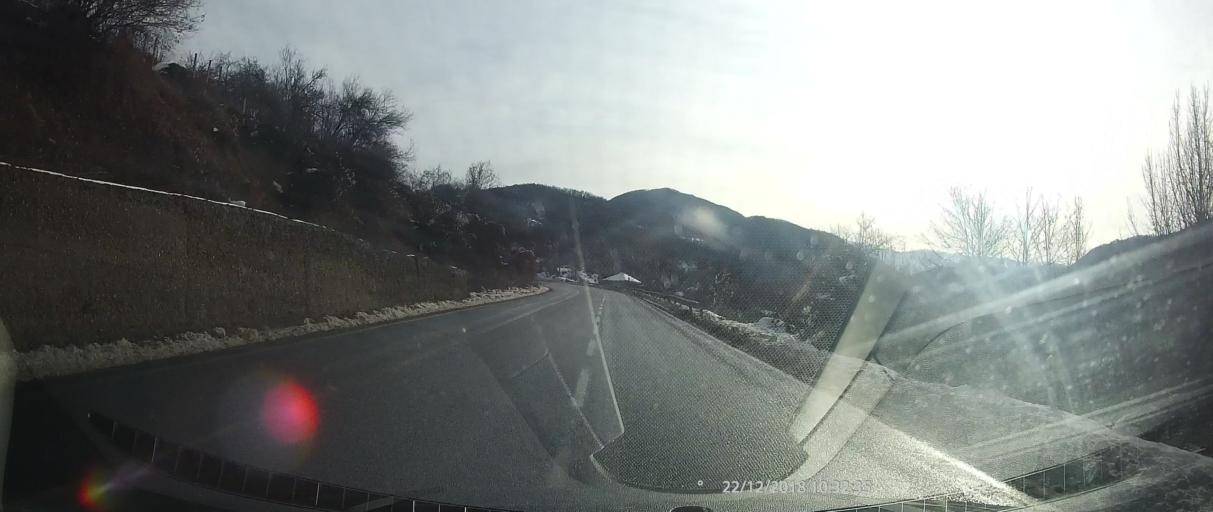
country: MK
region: Kriva Palanka
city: Kriva Palanka
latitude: 42.2186
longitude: 22.4354
